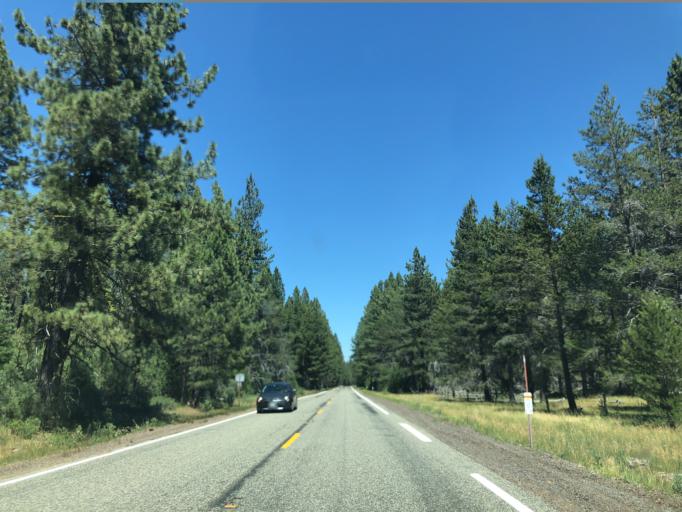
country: US
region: California
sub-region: Shasta County
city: Burney
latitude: 40.6075
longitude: -121.5211
